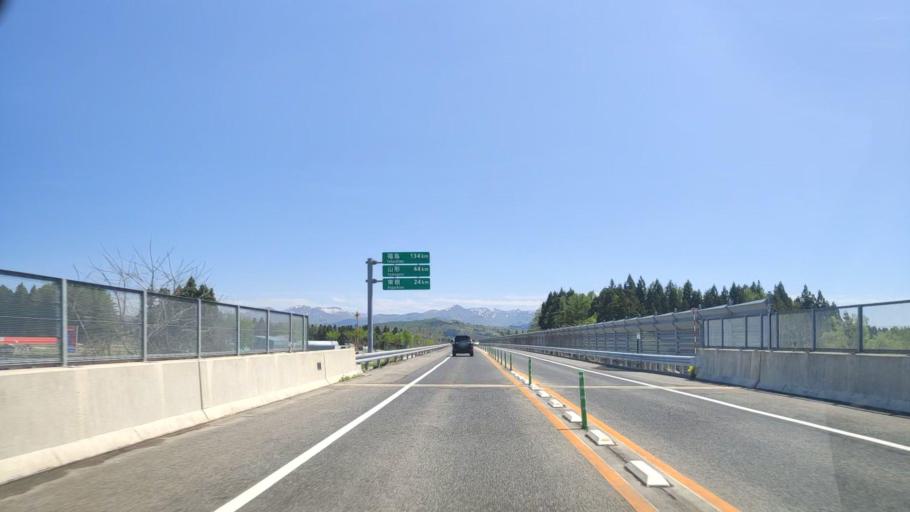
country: JP
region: Yamagata
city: Obanazawa
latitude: 38.6217
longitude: 140.3807
